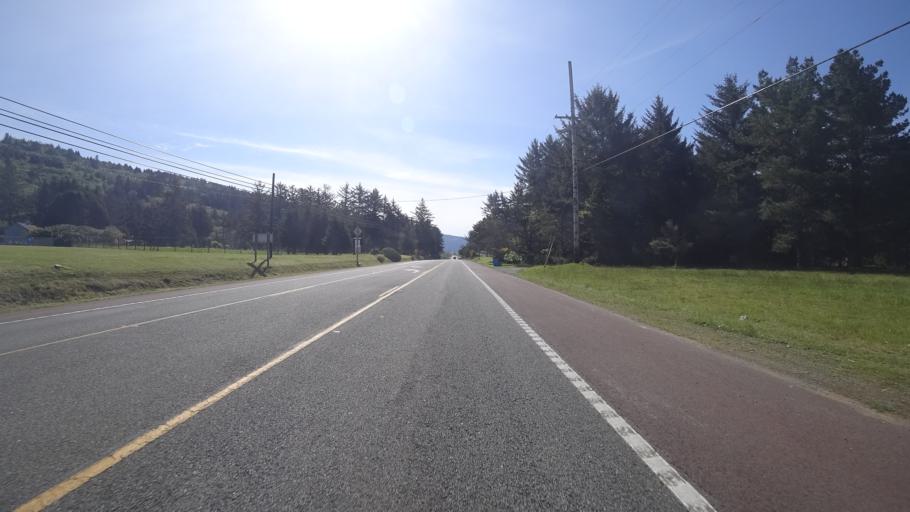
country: US
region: Oregon
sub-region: Curry County
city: Harbor
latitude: 41.9512
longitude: -124.2023
